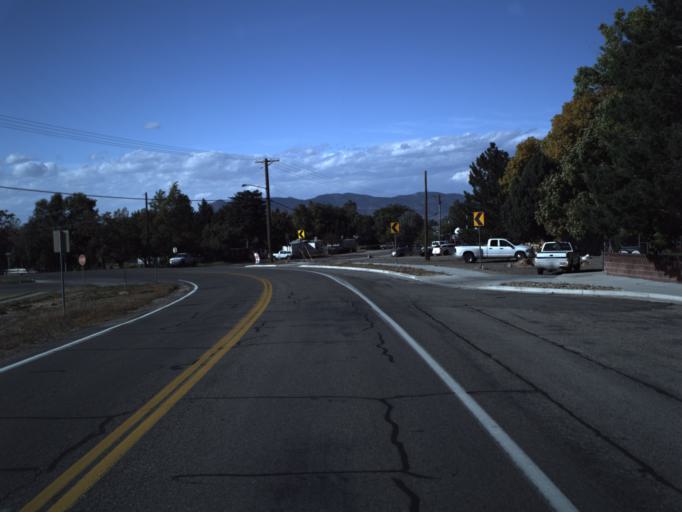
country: US
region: Utah
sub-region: Iron County
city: Parowan
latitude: 37.8414
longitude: -112.8209
